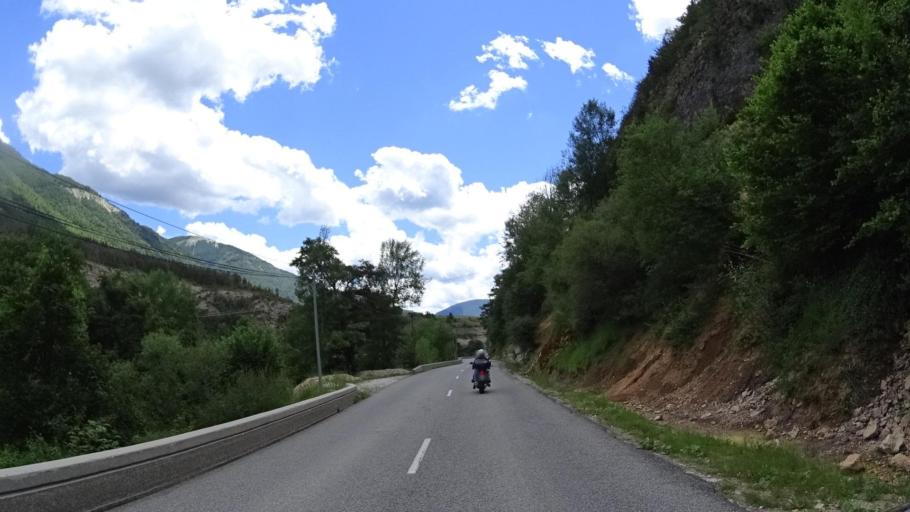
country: FR
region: Provence-Alpes-Cote d'Azur
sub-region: Departement des Alpes-de-Haute-Provence
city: Annot
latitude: 44.0163
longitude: 6.5585
